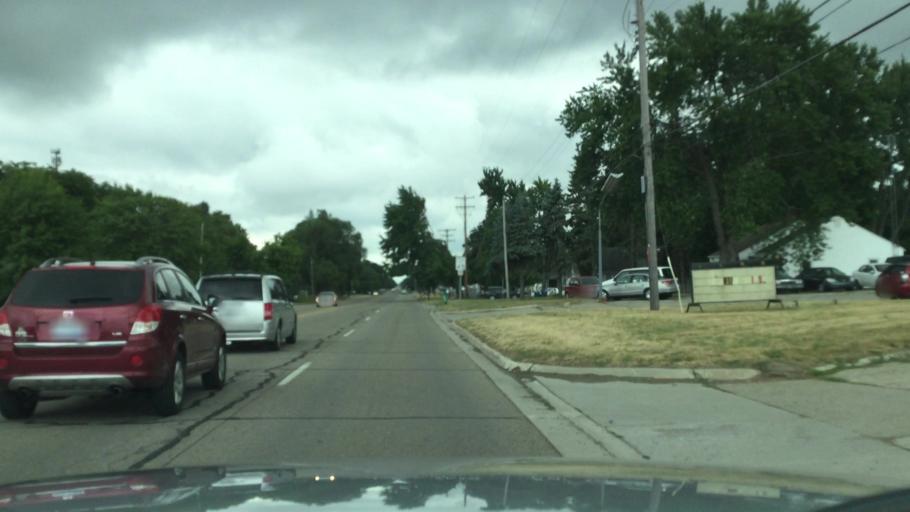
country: US
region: Michigan
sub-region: Genesee County
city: Beecher
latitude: 43.0839
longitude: -83.6170
